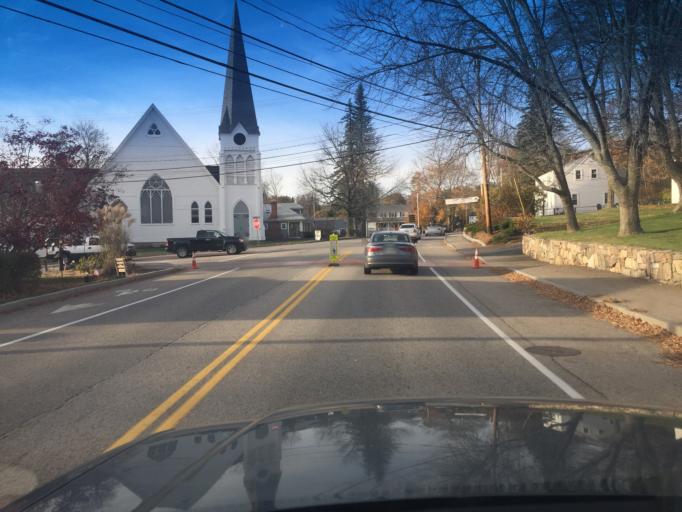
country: US
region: Maine
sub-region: York County
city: York Harbor
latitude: 43.1480
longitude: -70.6612
